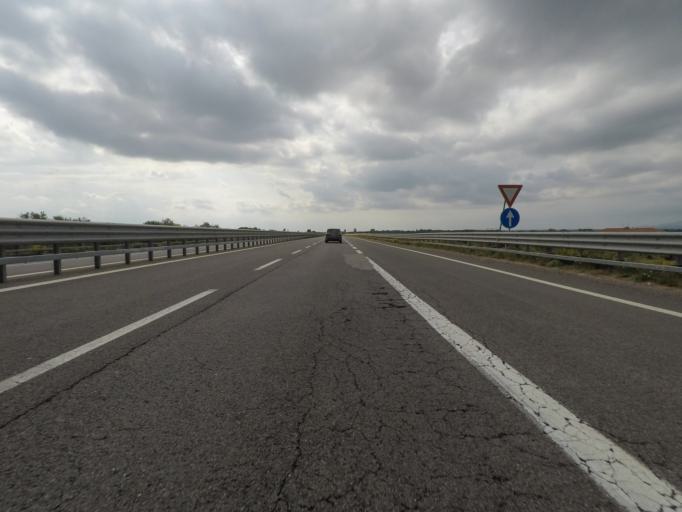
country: IT
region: Tuscany
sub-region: Provincia di Grosseto
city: Bagno Roselle
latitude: 42.8222
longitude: 11.1338
